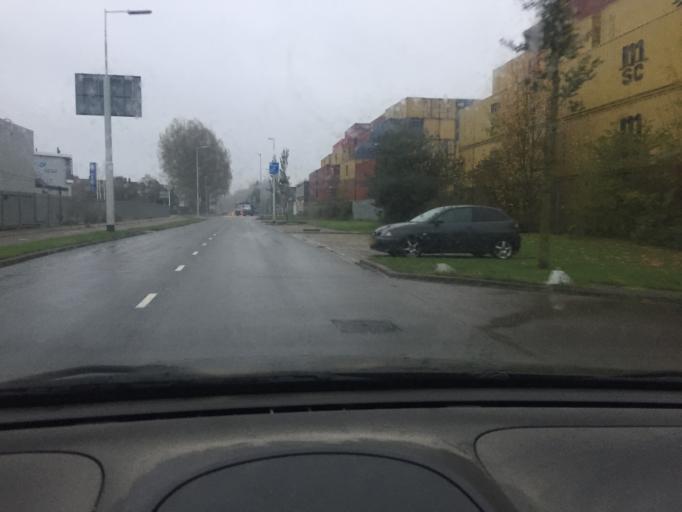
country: NL
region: South Holland
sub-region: Gemeente Albrandswaard
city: Rhoon
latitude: 51.8915
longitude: 4.4139
